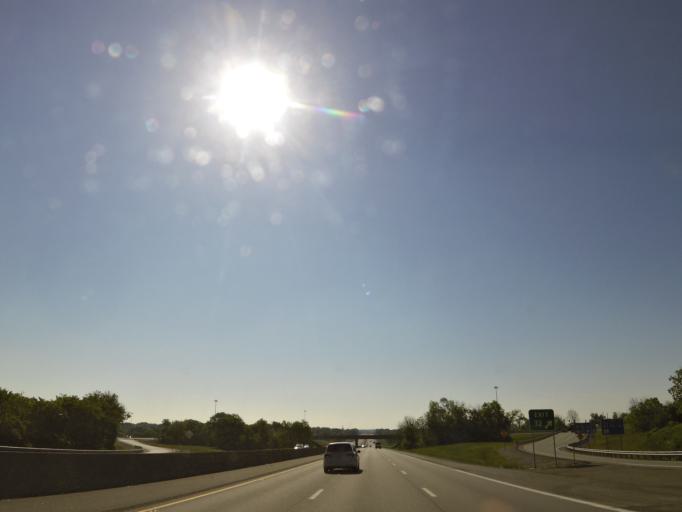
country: US
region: Kentucky
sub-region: Shelby County
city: Shelbyville
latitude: 38.1934
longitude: -85.2760
